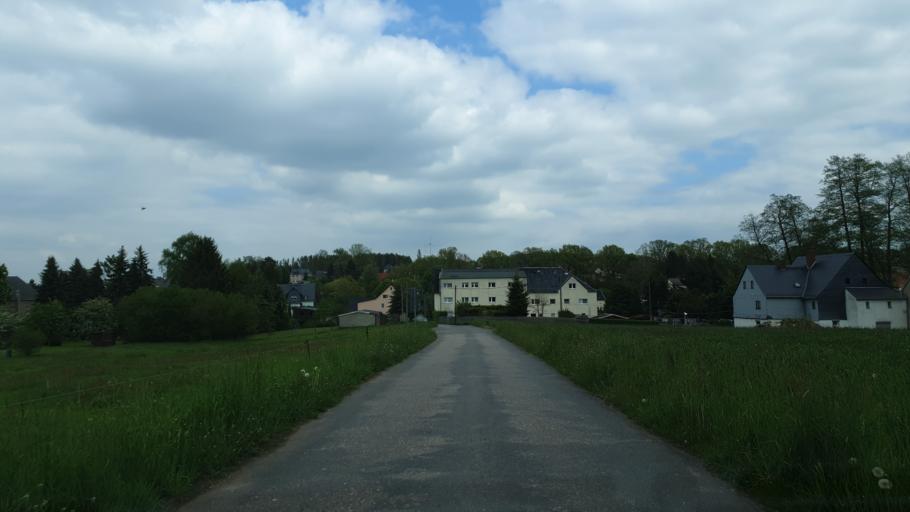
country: DE
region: Saxony
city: Oberlungwitz
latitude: 50.7677
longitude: 12.7025
